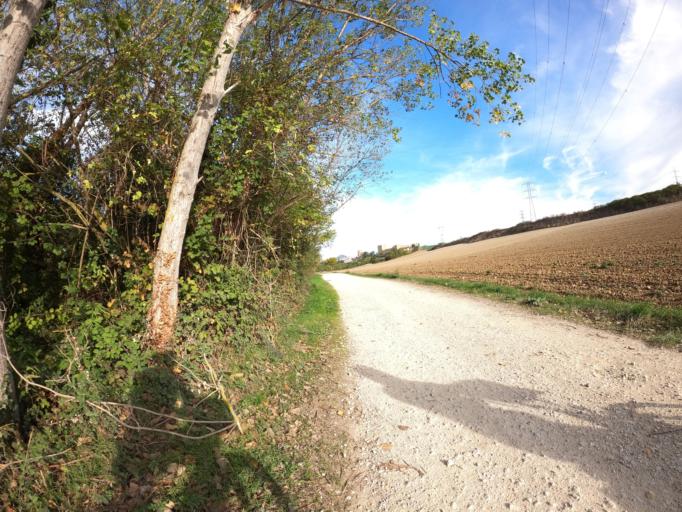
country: ES
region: Navarre
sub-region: Provincia de Navarra
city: Orkoien
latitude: 42.8093
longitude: -1.7154
